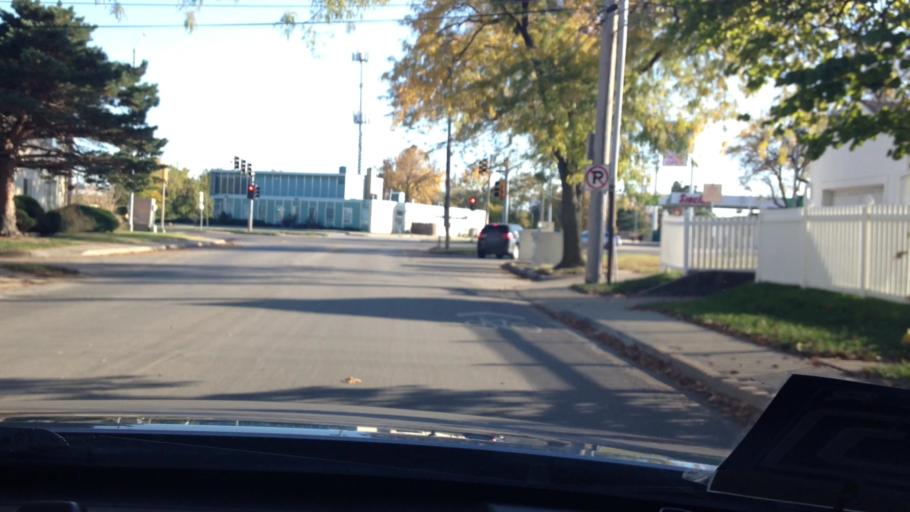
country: US
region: Missouri
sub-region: Clay County
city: North Kansas City
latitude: 39.1449
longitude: -94.5647
